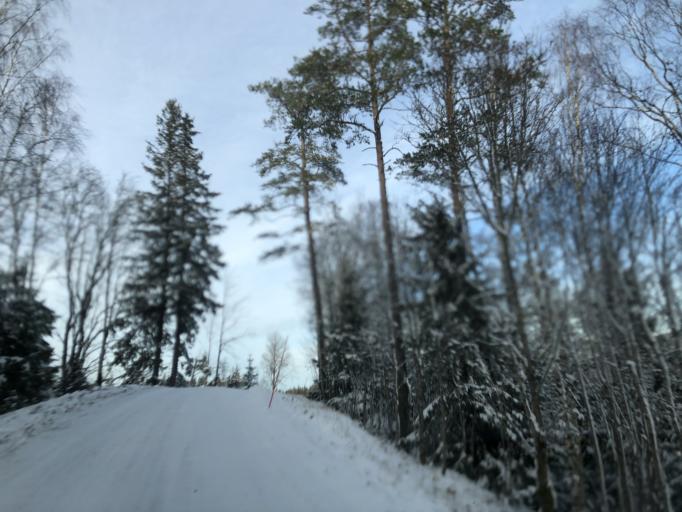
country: SE
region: Vaestra Goetaland
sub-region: Ulricehamns Kommun
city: Ulricehamn
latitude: 57.7693
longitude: 13.5215
